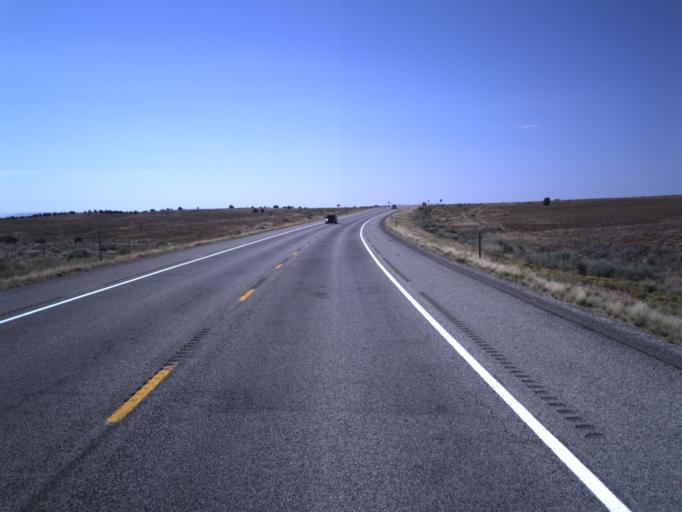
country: US
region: Utah
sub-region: San Juan County
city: Blanding
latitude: 37.4440
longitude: -109.4678
